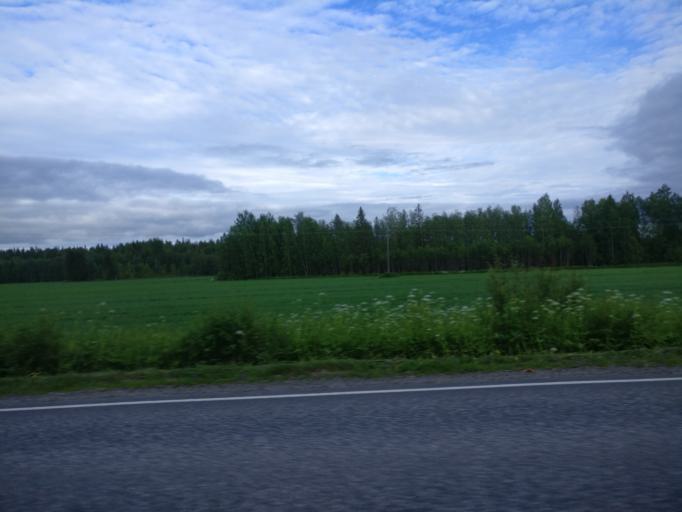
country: FI
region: Southern Savonia
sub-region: Savonlinna
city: Savonlinna
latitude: 61.9012
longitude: 28.9253
